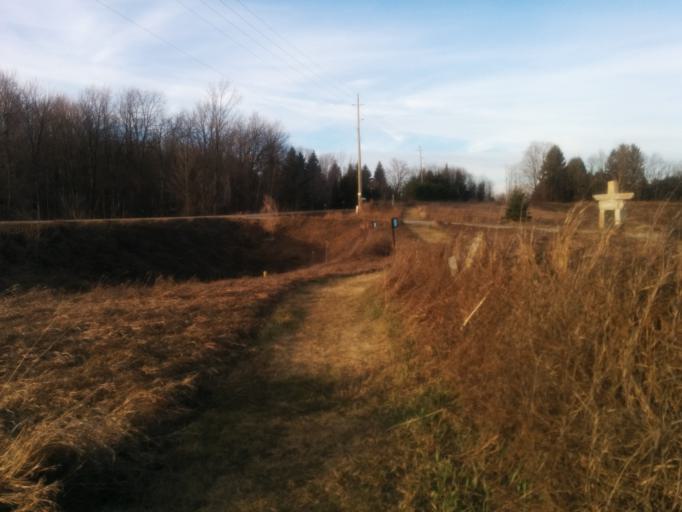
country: CA
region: Ontario
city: Orangeville
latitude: 43.9606
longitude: -79.9796
